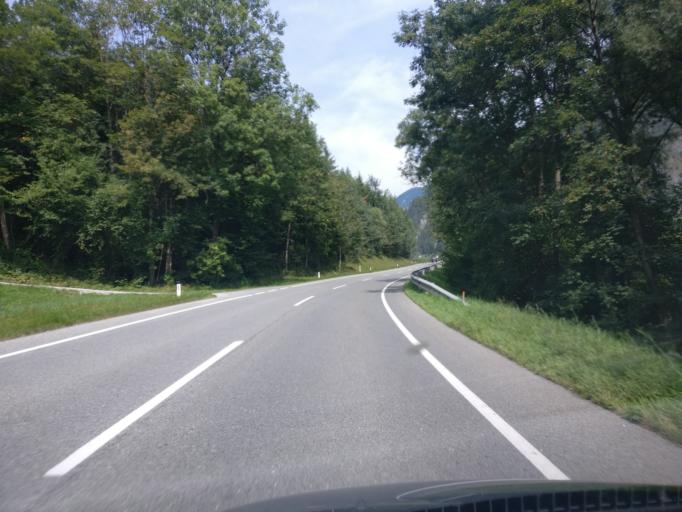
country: AT
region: Salzburg
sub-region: Politischer Bezirk Sankt Johann im Pongau
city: Werfen
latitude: 47.5073
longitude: 13.1664
